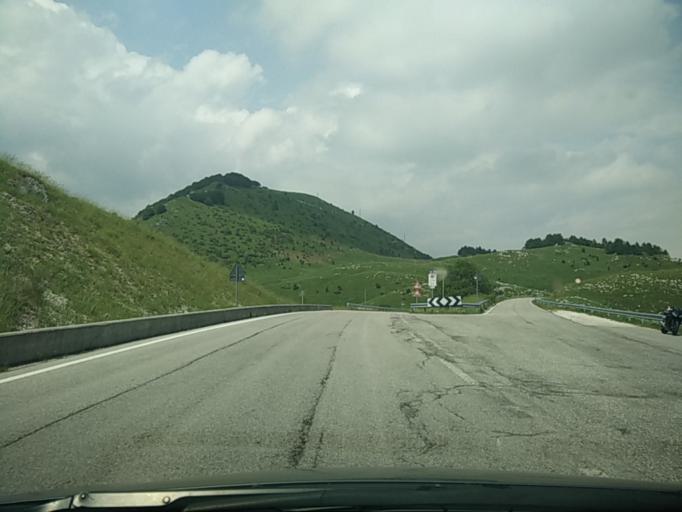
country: IT
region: Friuli Venezia Giulia
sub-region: Provincia di Pordenone
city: Budoia
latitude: 46.0866
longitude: 12.5279
